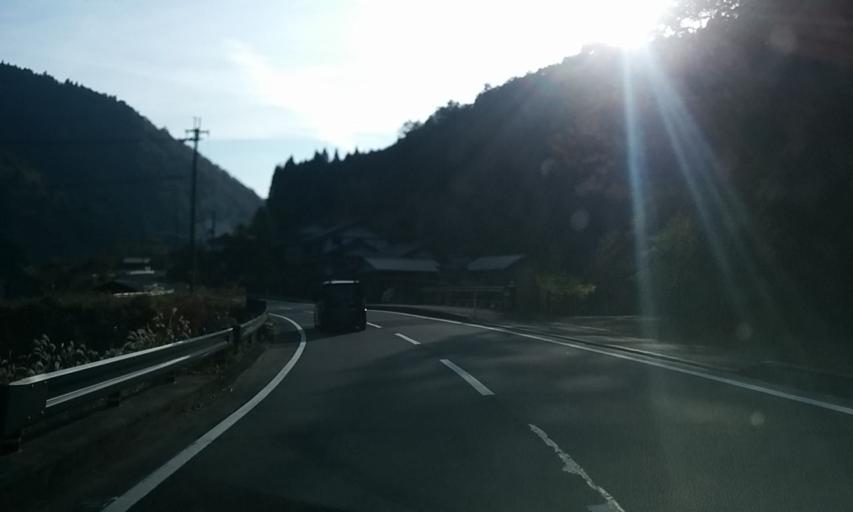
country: JP
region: Fukui
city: Obama
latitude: 35.2904
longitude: 135.6001
